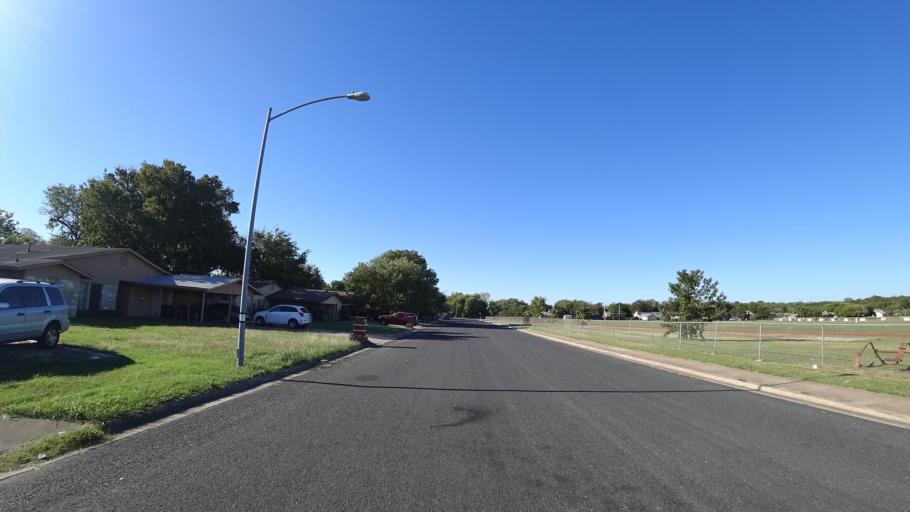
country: US
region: Texas
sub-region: Travis County
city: Hornsby Bend
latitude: 30.3110
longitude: -97.6541
